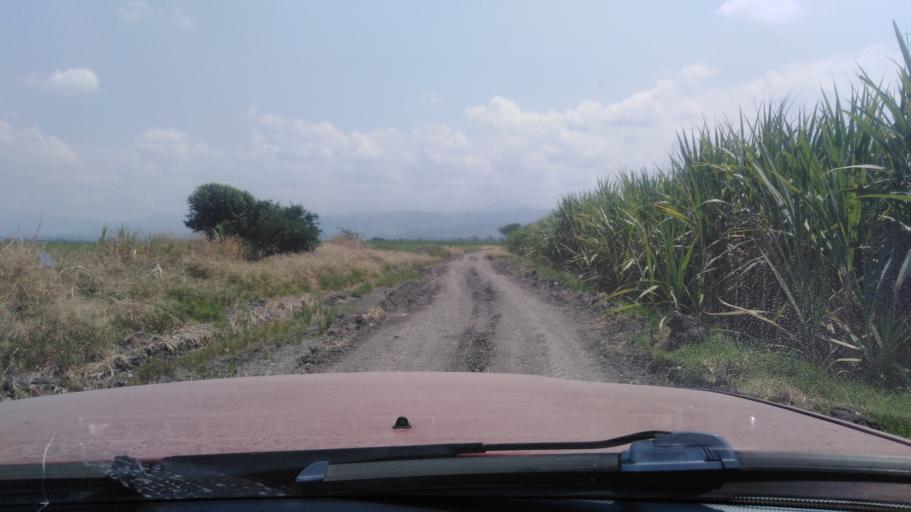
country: CO
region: Valle del Cauca
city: San Pedro
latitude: 3.9992
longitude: -76.2776
